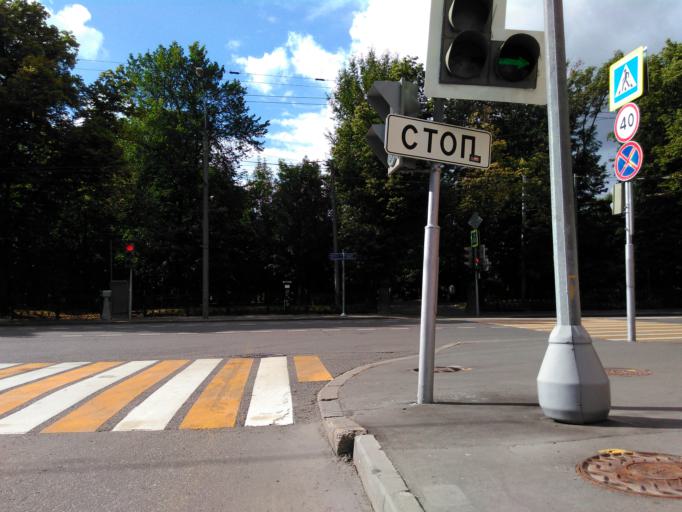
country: RU
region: Moskovskaya
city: Dorogomilovo
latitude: 55.7337
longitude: 37.5756
